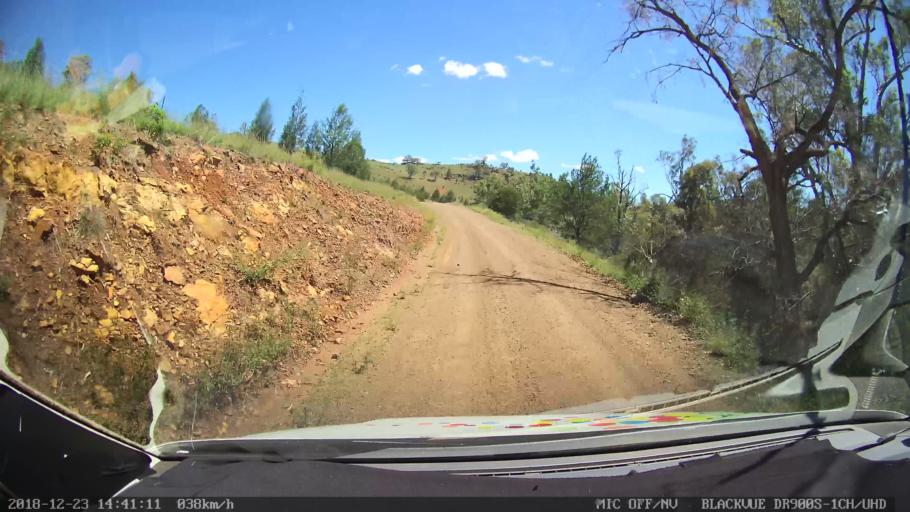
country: AU
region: New South Wales
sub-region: Tamworth Municipality
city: Manilla
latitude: -30.6300
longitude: 150.9026
